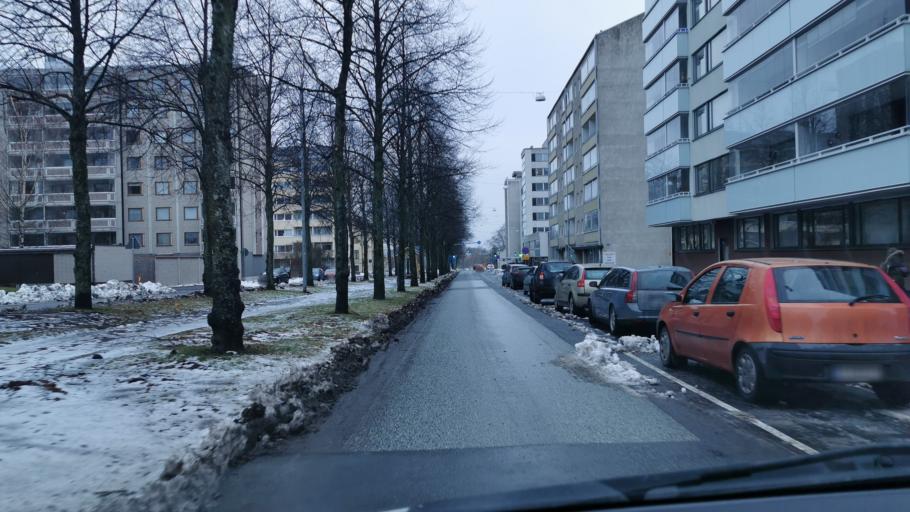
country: FI
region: Ostrobothnia
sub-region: Vaasa
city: Vaasa
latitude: 63.0984
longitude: 21.6070
